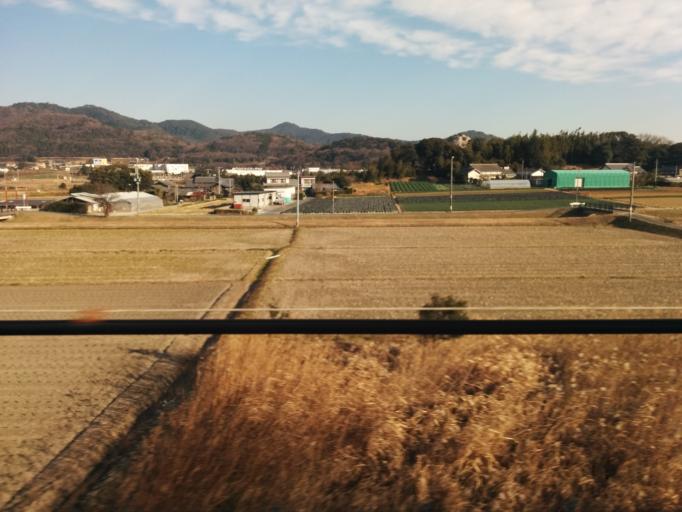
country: JP
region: Shizuoka
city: Kosai-shi
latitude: 34.7191
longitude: 137.4661
